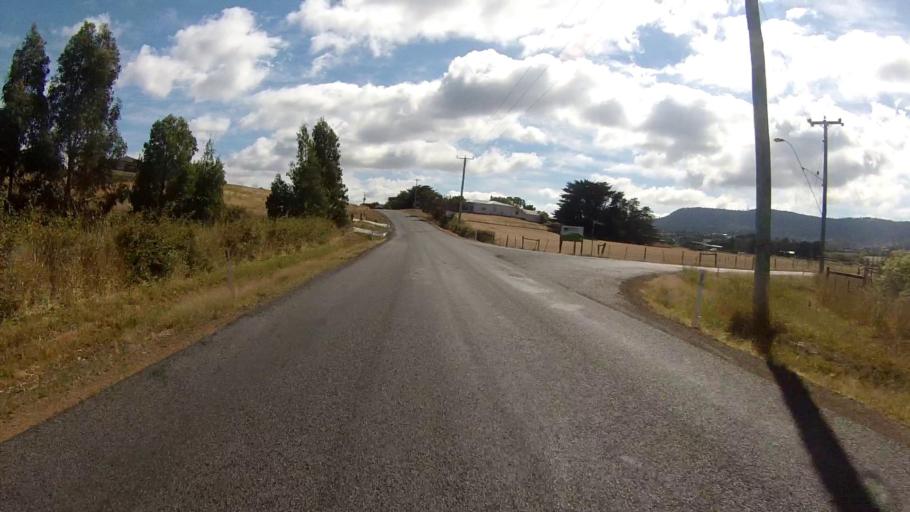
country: AU
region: Tasmania
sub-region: Brighton
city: Old Beach
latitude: -42.7642
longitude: 147.2773
